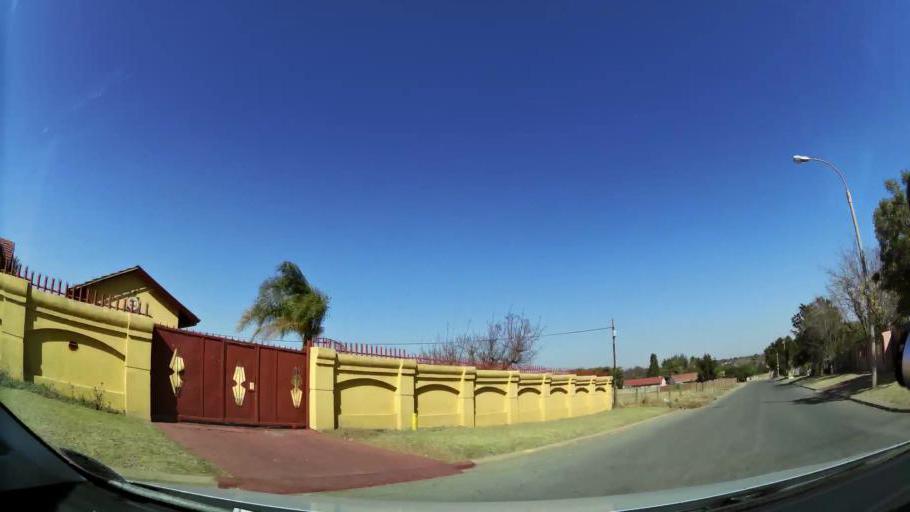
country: ZA
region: Gauteng
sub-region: Ekurhuleni Metropolitan Municipality
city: Tembisa
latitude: -26.0344
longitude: 28.2320
